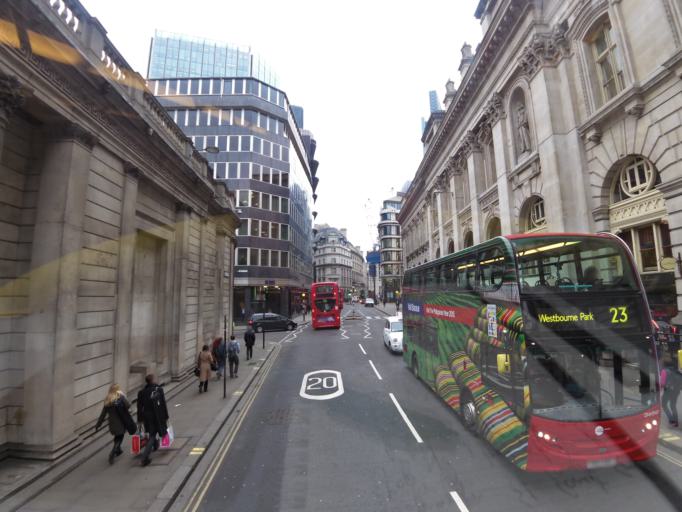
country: GB
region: England
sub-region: Greater London
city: City of London
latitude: 51.5136
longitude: -0.0875
